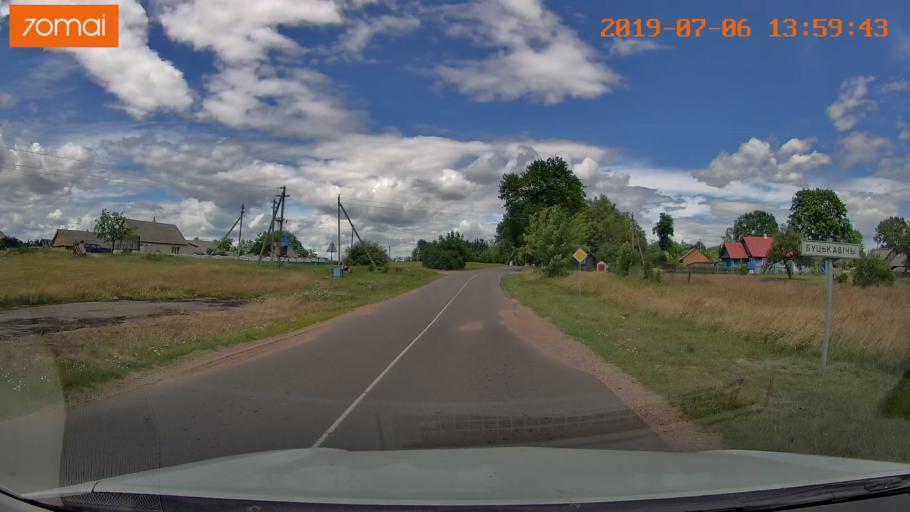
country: BY
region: Minsk
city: Ivyanyets
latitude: 53.7970
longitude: 26.8161
